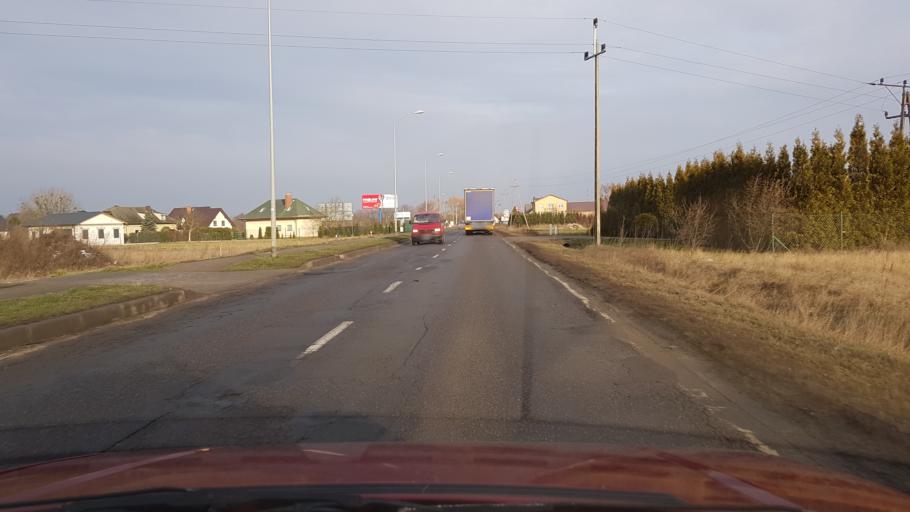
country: PL
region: West Pomeranian Voivodeship
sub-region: Powiat policki
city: Police
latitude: 53.5120
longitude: 14.5686
